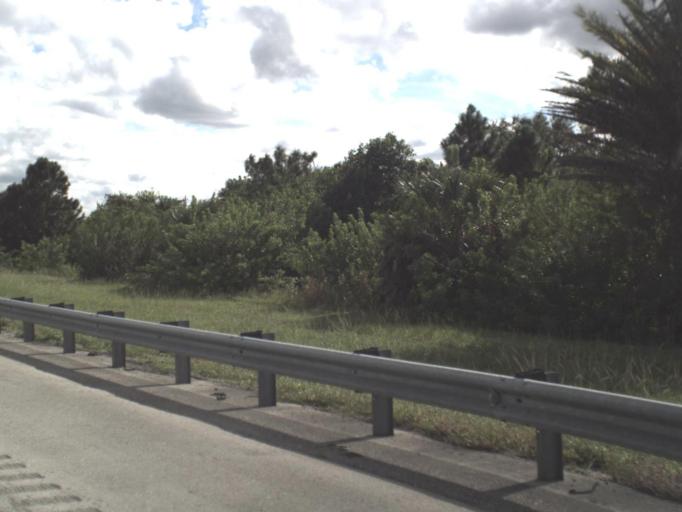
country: US
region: Florida
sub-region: Saint Lucie County
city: Port Saint Lucie
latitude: 27.2944
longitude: -80.3703
